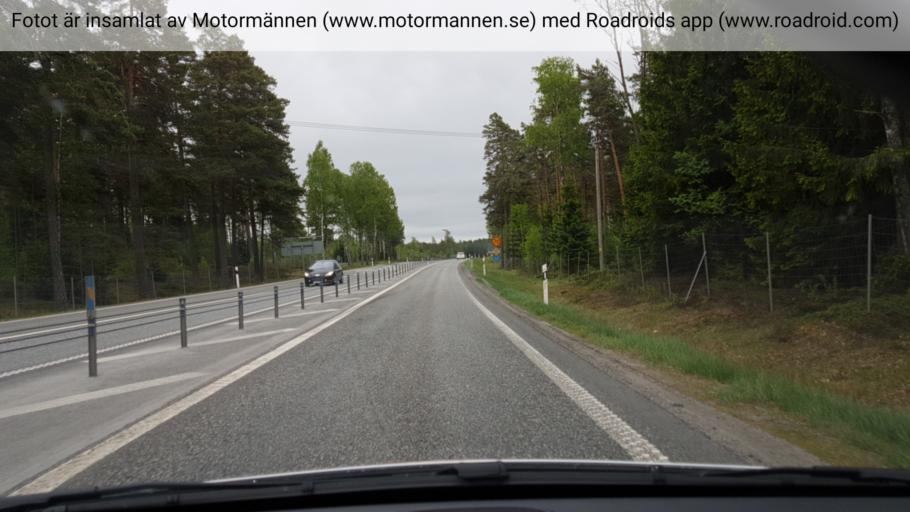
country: SE
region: Joenkoeping
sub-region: Mullsjo Kommun
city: Mullsjoe
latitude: 57.7635
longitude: 13.8296
